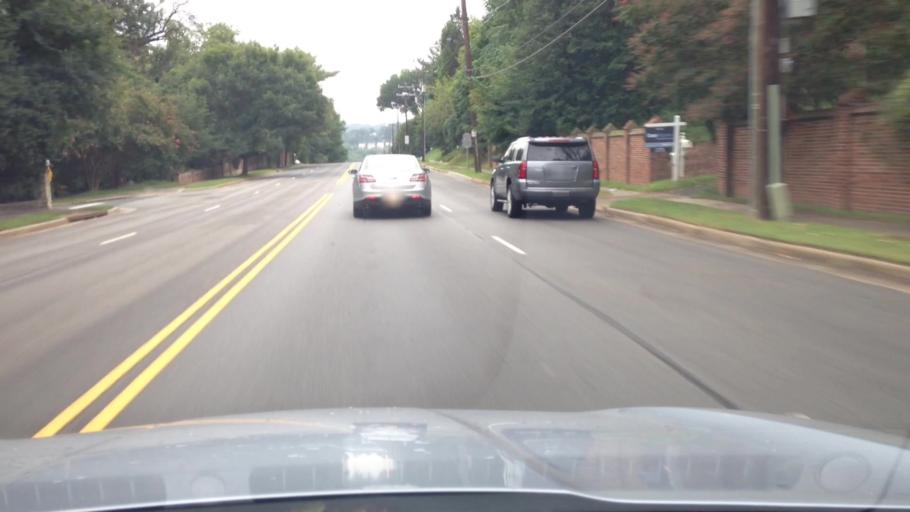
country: US
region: Virginia
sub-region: Fairfax County
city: Huntington
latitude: 38.8125
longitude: -77.0891
